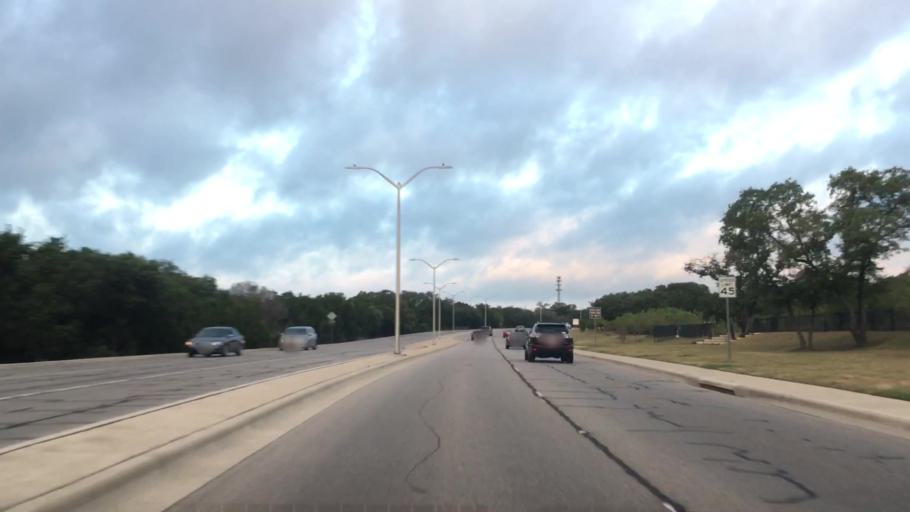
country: US
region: Texas
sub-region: Williamson County
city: Brushy Creek
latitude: 30.5072
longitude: -97.7775
